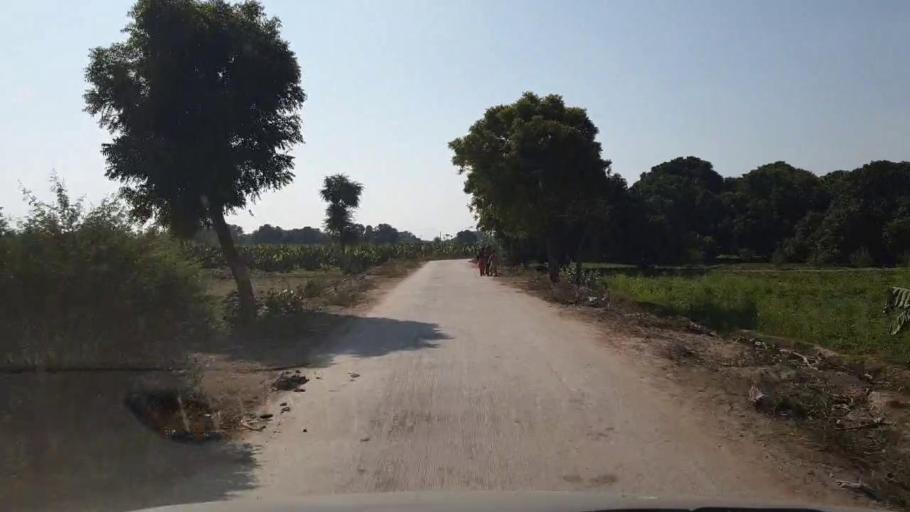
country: PK
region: Sindh
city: Tando Jam
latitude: 25.4475
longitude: 68.6243
